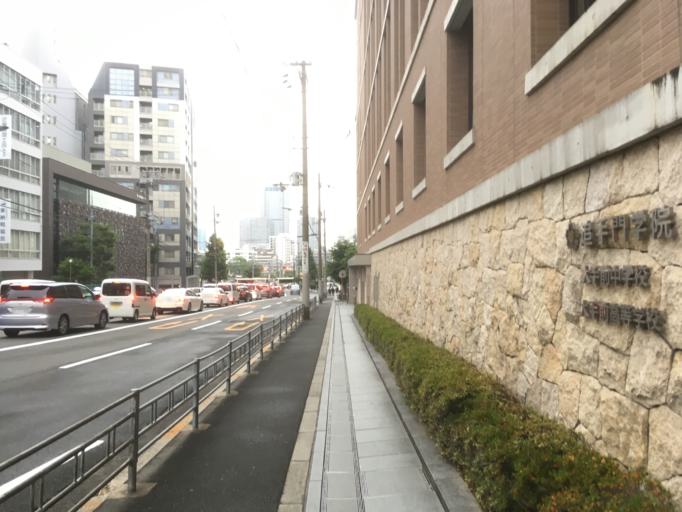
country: JP
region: Osaka
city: Osaka-shi
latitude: 34.6891
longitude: 135.5205
